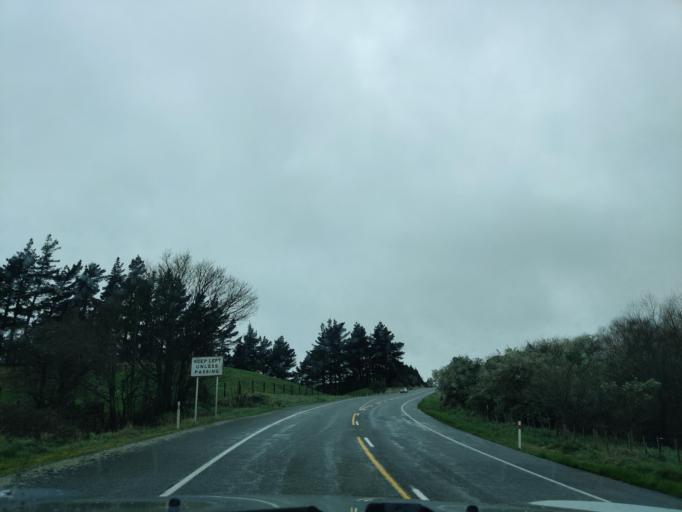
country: NZ
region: Manawatu-Wanganui
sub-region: Palmerston North City
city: Palmerston North
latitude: -40.0815
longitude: 176.1965
